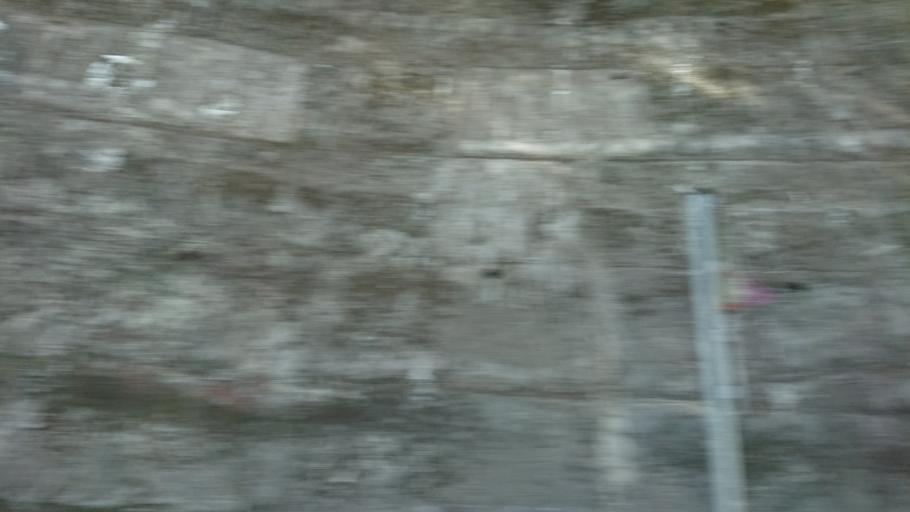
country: TW
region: Taiwan
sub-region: Hualien
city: Hualian
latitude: 24.3483
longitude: 121.3077
